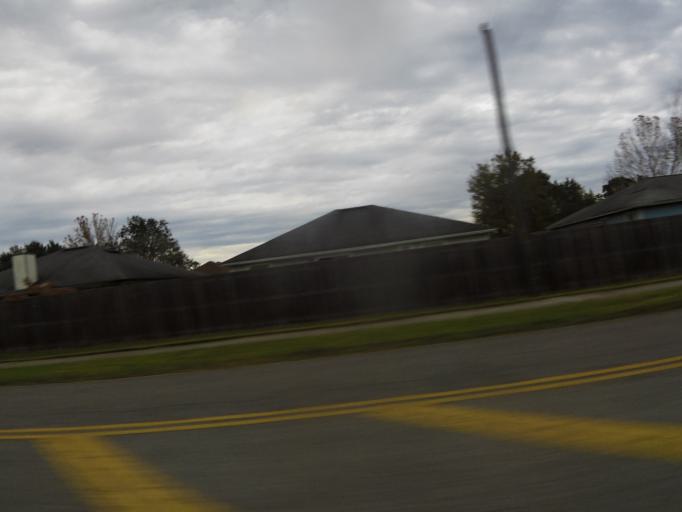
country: US
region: Florida
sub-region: Duval County
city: Jacksonville
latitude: 30.2642
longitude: -81.5858
